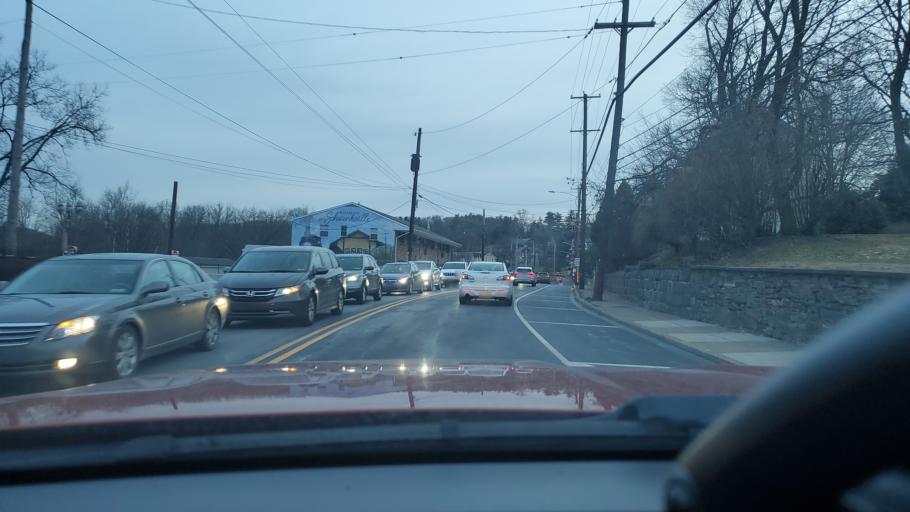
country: US
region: Pennsylvania
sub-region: Montgomery County
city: Schwenksville
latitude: 40.2562
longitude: -75.4637
